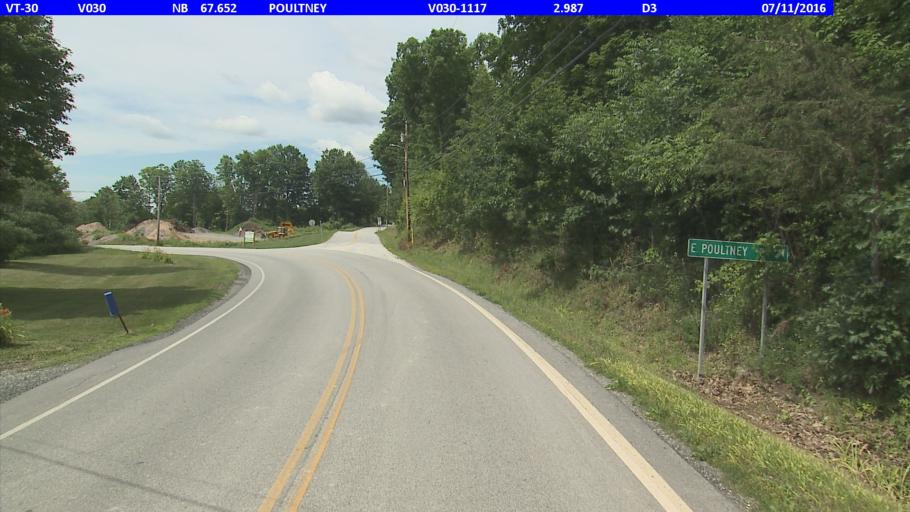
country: US
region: Vermont
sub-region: Rutland County
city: Poultney
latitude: 43.5045
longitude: -73.2098
